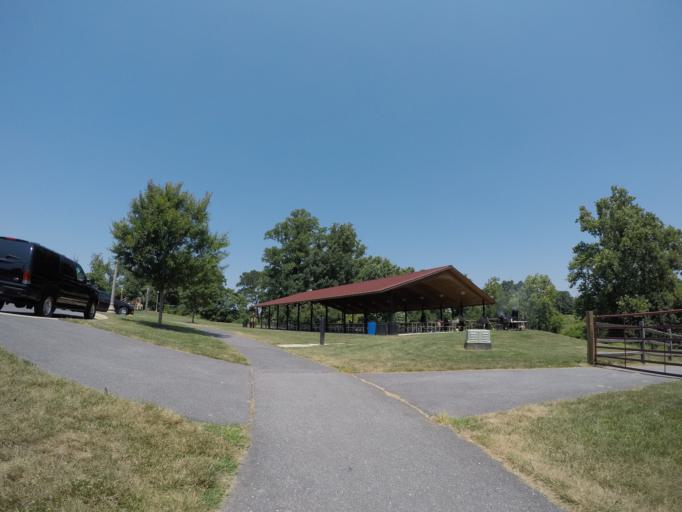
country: US
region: Maryland
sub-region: Frederick County
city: Urbana
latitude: 39.3400
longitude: -77.3648
